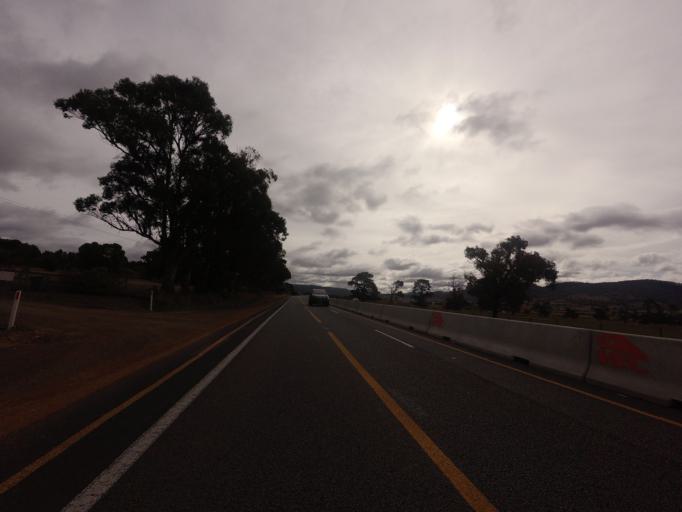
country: AU
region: Tasmania
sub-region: Brighton
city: Bridgewater
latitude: -42.6654
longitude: 147.2511
